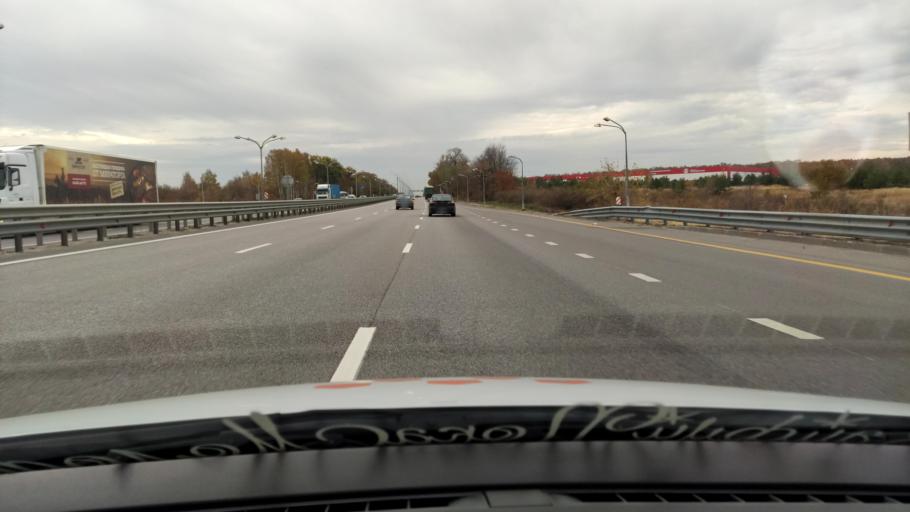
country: RU
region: Voronezj
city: Podgornoye
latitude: 51.8247
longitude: 39.2107
